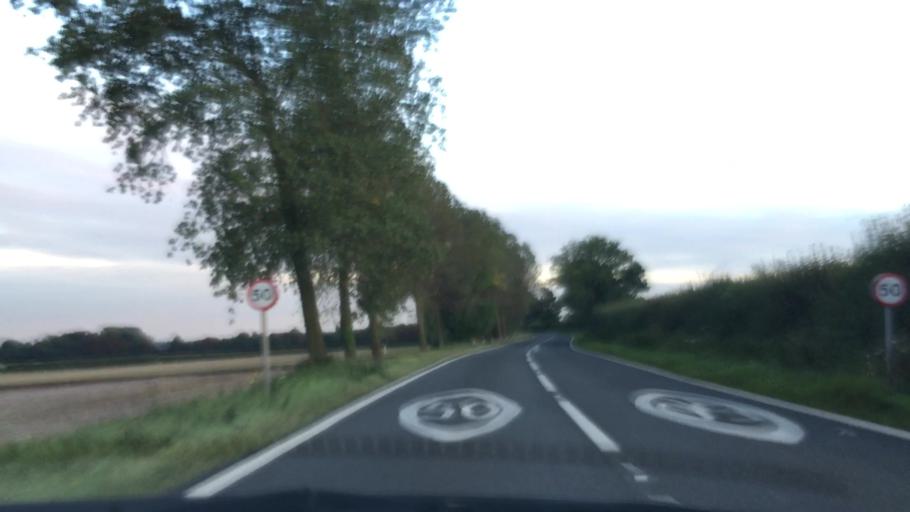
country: GB
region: England
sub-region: North East Lincolnshire
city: Wold Newton
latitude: 53.4712
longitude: -0.1094
